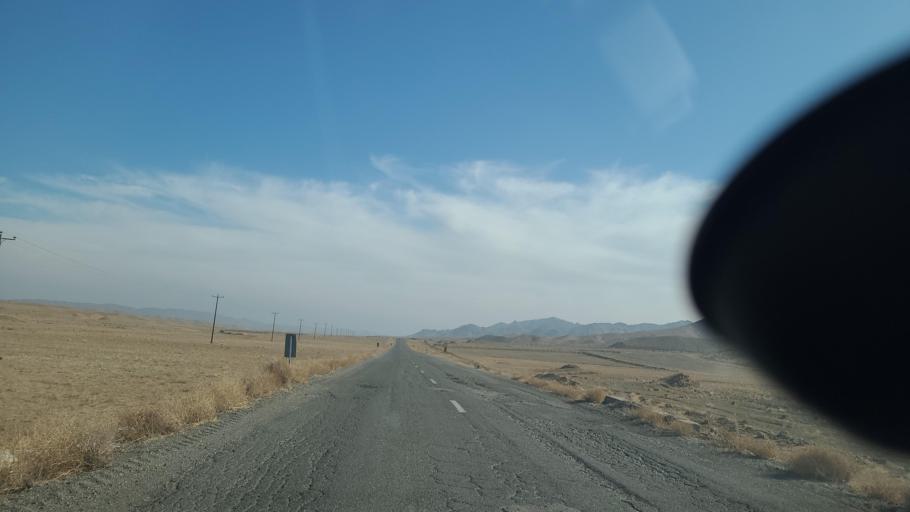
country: IR
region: Razavi Khorasan
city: Fariman
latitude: 35.5881
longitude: 59.6335
